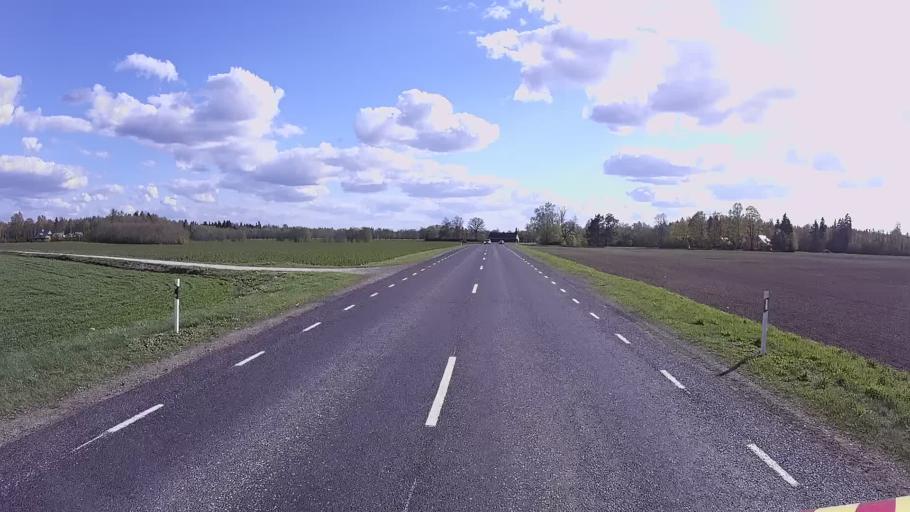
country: EE
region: Jogevamaa
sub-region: Jogeva linn
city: Jogeva
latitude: 58.7214
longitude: 26.1882
